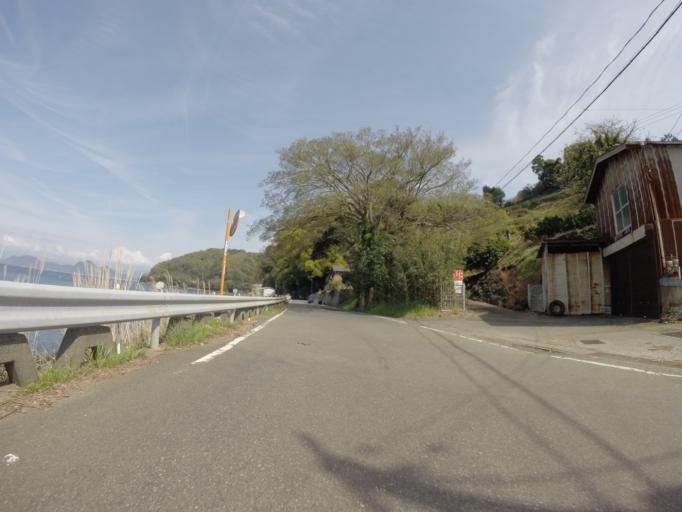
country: JP
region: Shizuoka
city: Heda
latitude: 35.0207
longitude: 138.8056
